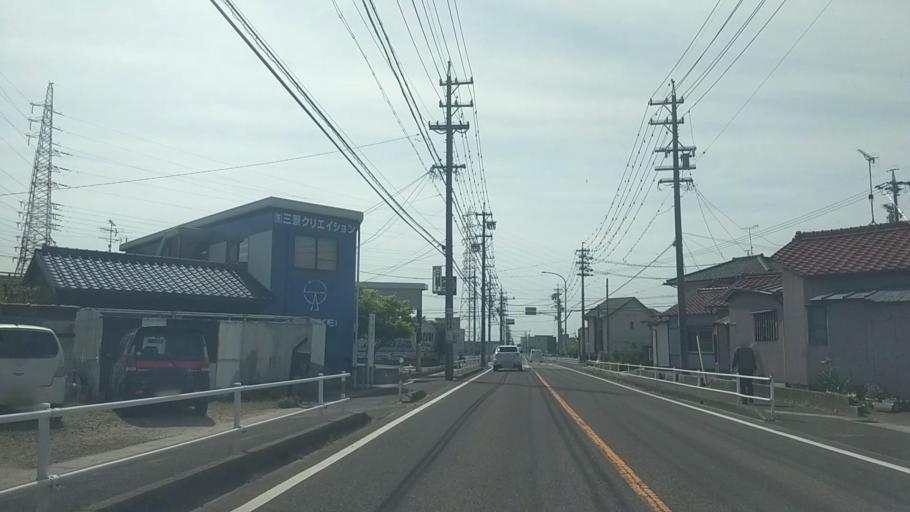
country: JP
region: Aichi
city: Anjo
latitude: 34.9585
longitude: 137.0644
